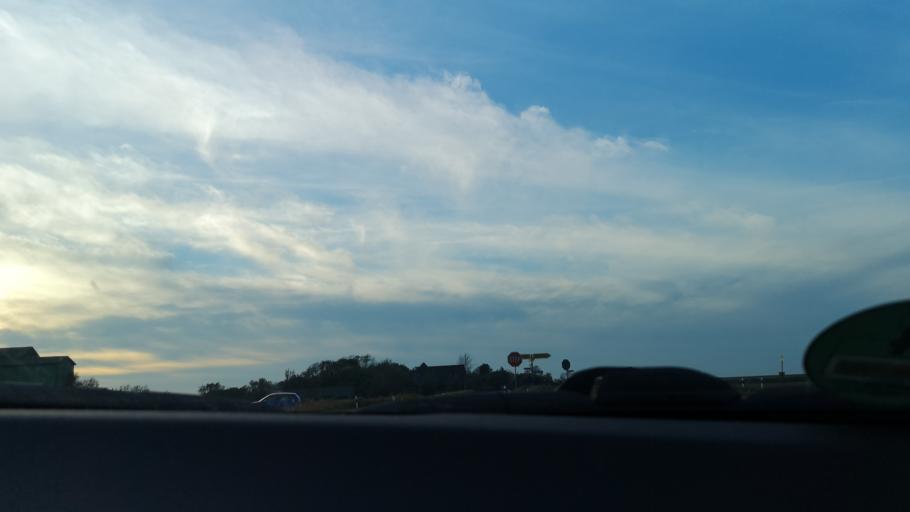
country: DE
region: Schleswig-Holstein
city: Pellworm
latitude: 54.5161
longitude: 8.6134
